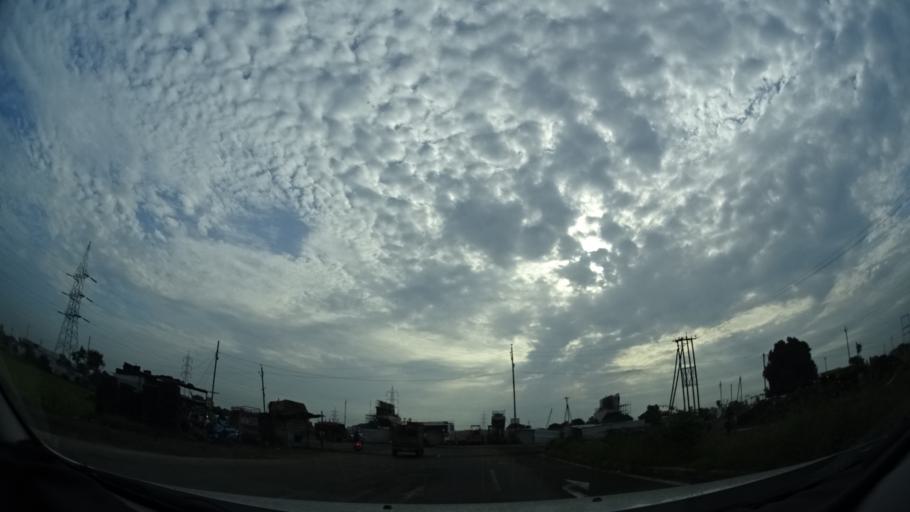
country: IN
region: Madhya Pradesh
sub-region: Bhopal
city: Bhopal
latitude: 23.3387
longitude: 77.4001
